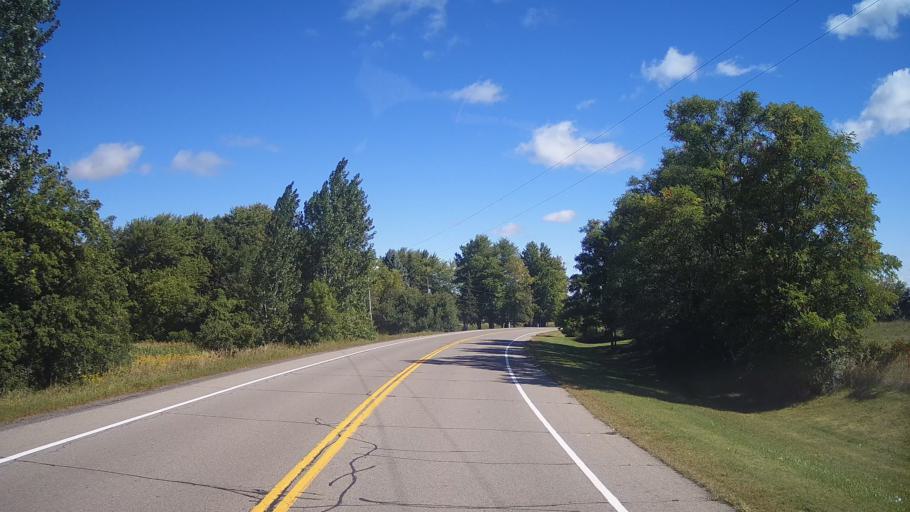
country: US
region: New York
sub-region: St. Lawrence County
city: Norfolk
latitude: 44.9617
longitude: -75.2825
